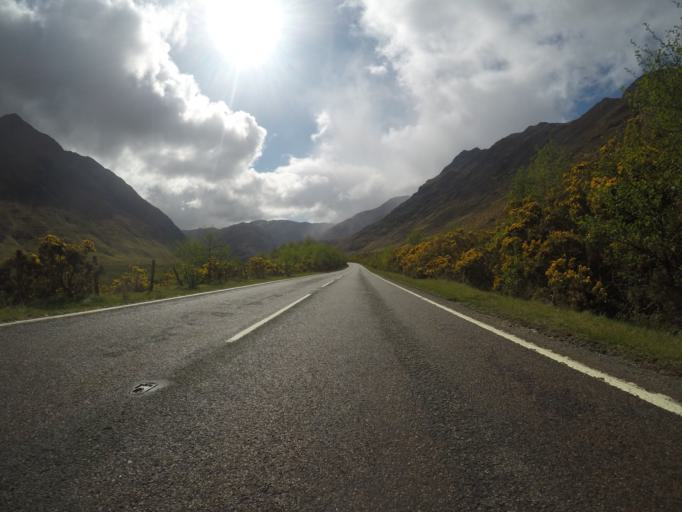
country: GB
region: Scotland
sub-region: Highland
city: Fort William
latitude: 57.1932
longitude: -5.3874
